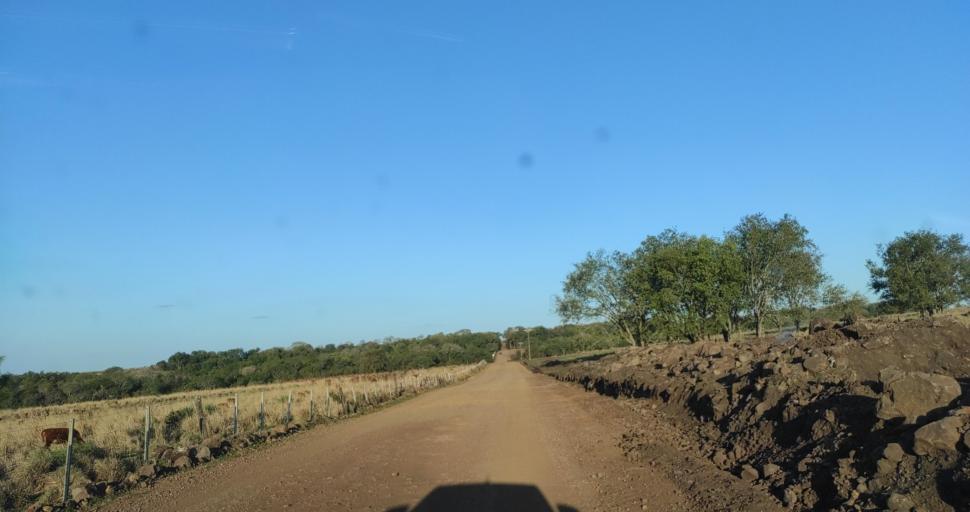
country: PY
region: Itapua
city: San Juan del Parana
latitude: -27.4169
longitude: -56.1301
